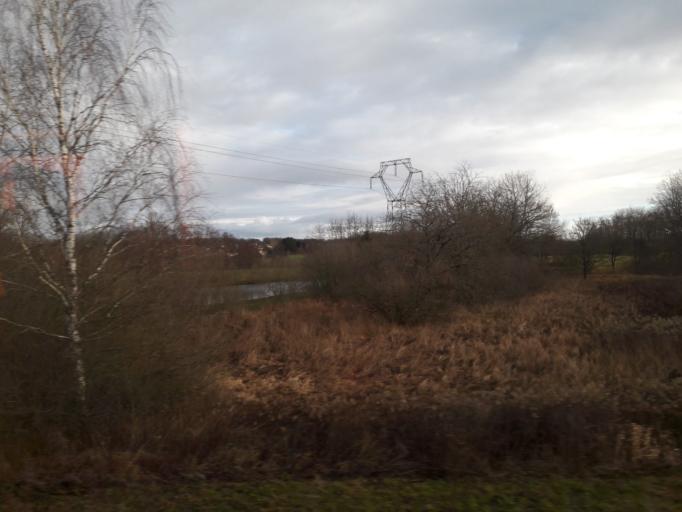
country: FR
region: Franche-Comte
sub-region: Territoire de Belfort
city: Joncherey
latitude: 47.5199
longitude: 7.0028
